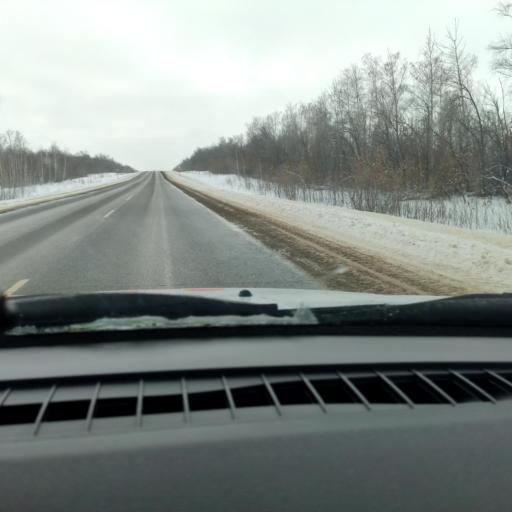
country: RU
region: Samara
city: Dubovyy Umet
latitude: 52.7498
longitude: 50.4927
